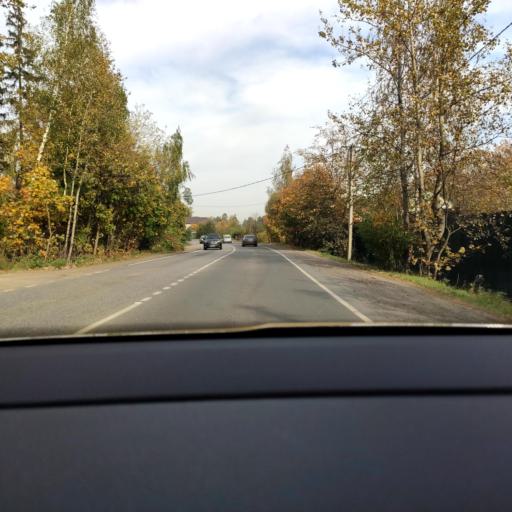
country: RU
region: Moskovskaya
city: Lesnyye Polyany
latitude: 55.9692
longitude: 37.8716
